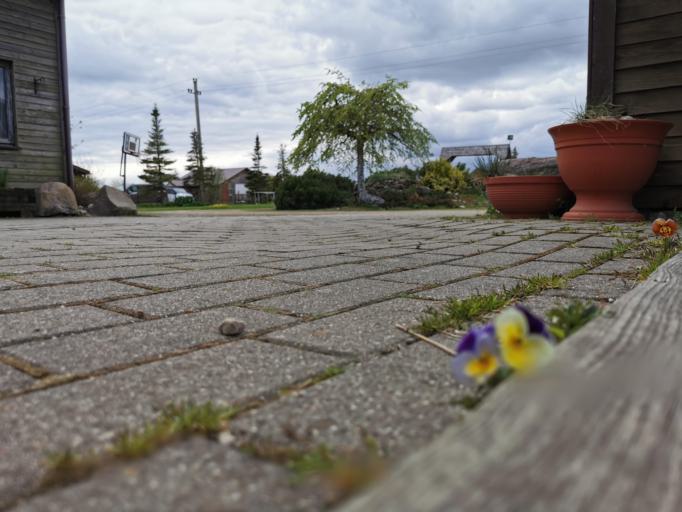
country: LT
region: Kauno apskritis
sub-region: Kauno rajonas
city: Akademija (Kaunas)
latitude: 55.0089
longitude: 23.7744
